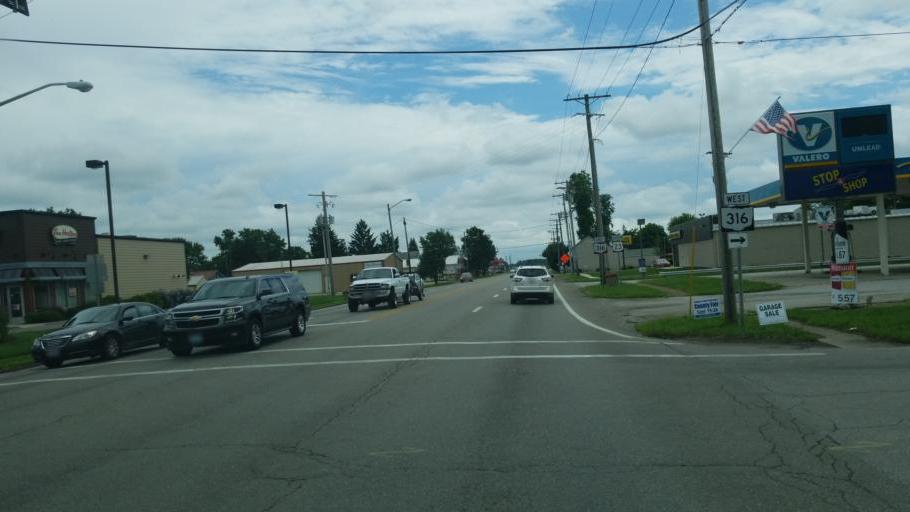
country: US
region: Ohio
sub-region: Pickaway County
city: South Bloomfield
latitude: 39.7187
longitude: -82.9868
